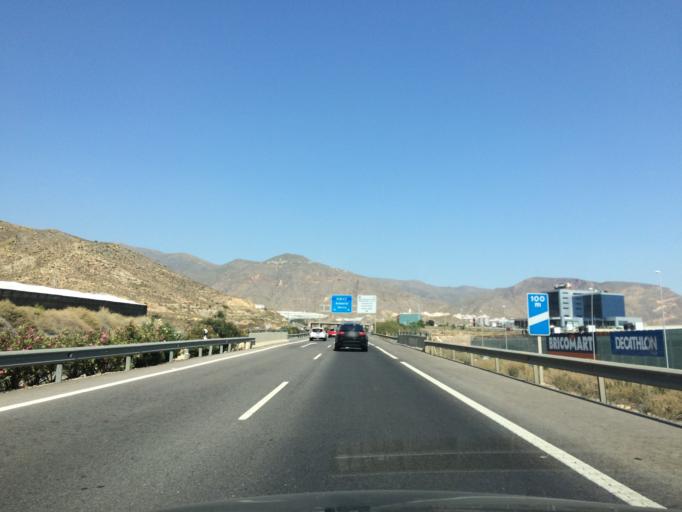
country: ES
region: Andalusia
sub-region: Provincia de Almeria
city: Aguadulce
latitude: 36.8171
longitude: -2.6024
